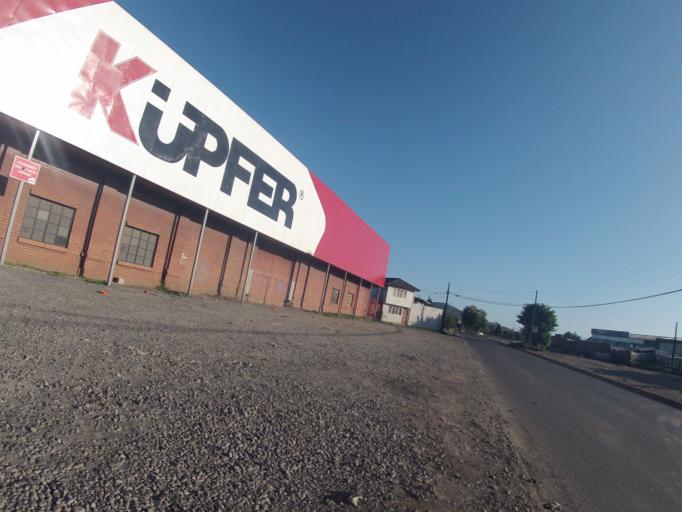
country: CL
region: Araucania
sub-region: Provincia de Cautin
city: Temuco
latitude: -38.7279
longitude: -72.5780
